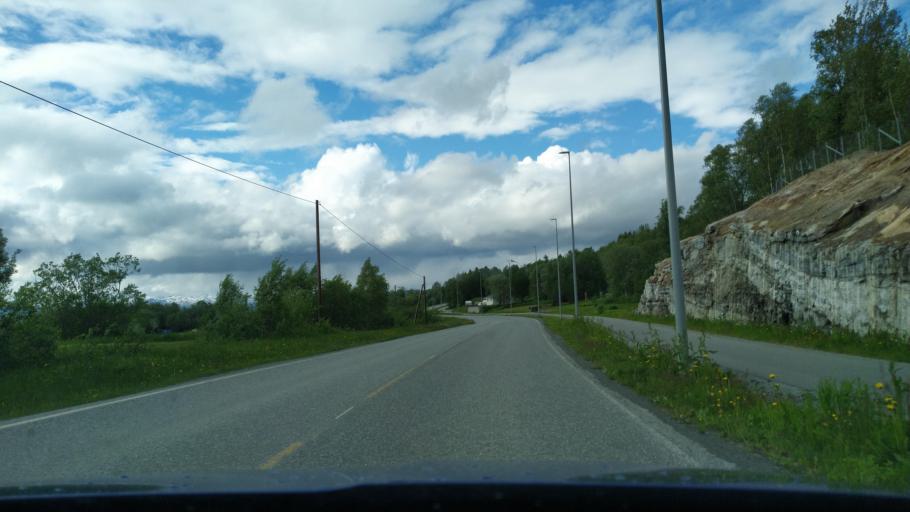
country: NO
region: Troms
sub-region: Lenvik
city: Finnsnes
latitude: 69.1800
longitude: 18.0578
